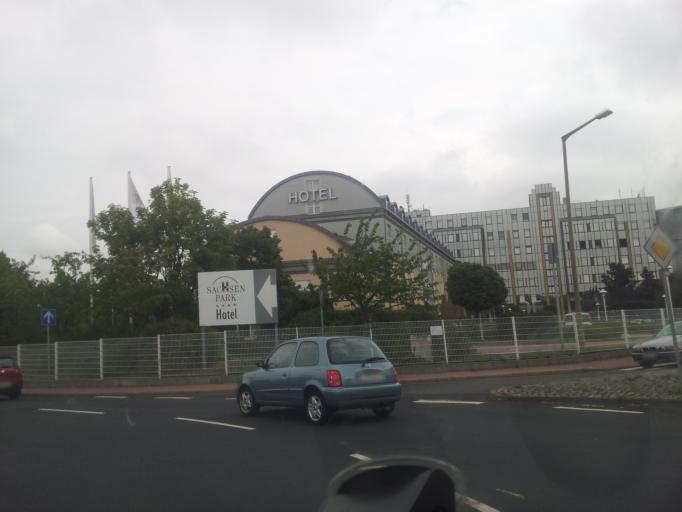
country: DE
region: Saxony
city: Rackwitz
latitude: 51.3995
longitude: 12.4014
